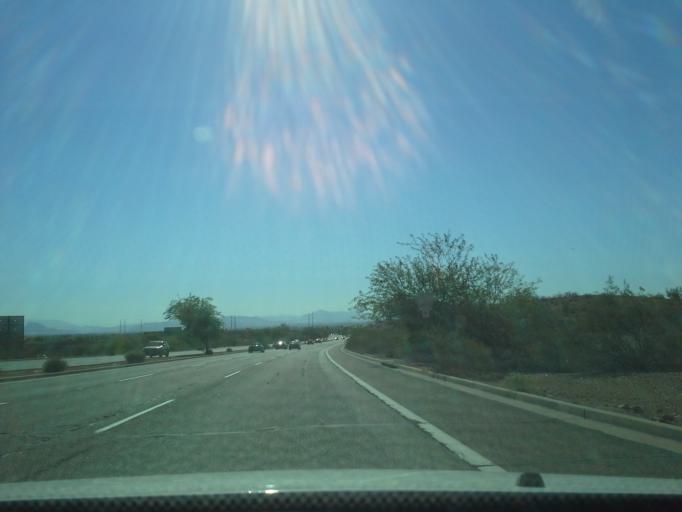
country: US
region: Arizona
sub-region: Maricopa County
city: Tempe Junction
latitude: 33.4663
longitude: -111.9489
